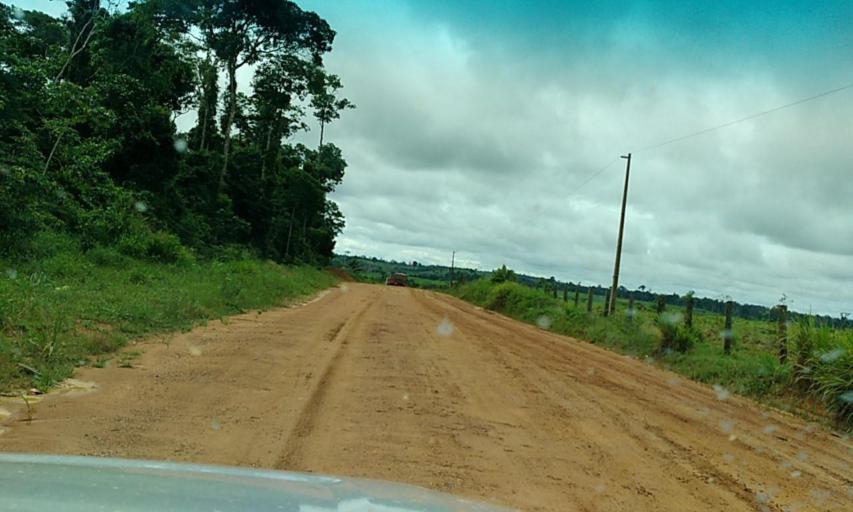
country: BR
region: Para
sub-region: Altamira
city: Altamira
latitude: -3.0648
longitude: -51.7110
